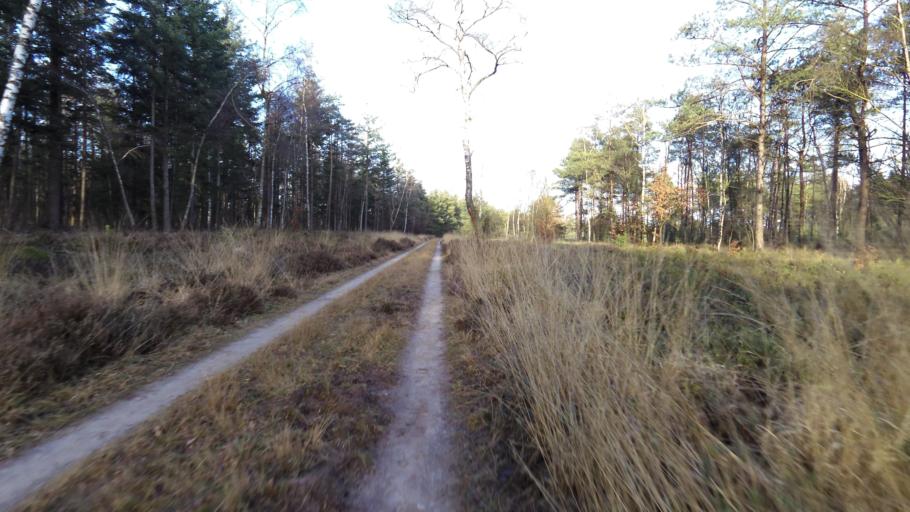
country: NL
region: Gelderland
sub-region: Gemeente Epe
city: Vaassen
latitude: 52.2733
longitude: 5.9095
